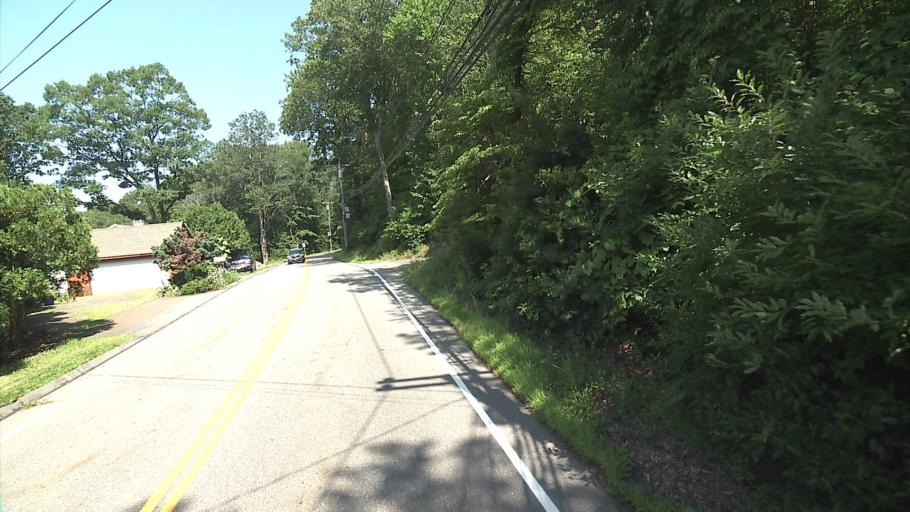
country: US
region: Connecticut
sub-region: New Haven County
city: North Branford
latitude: 41.2803
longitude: -72.7615
